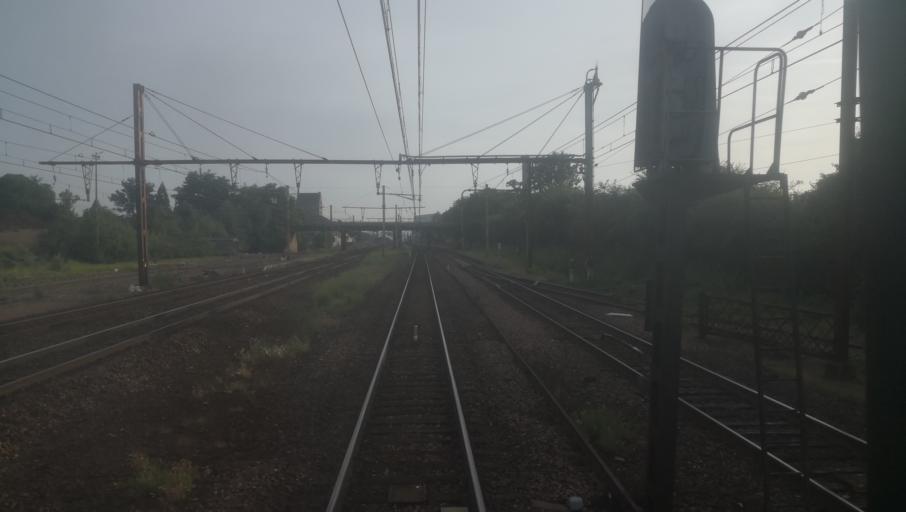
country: FR
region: Centre
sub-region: Departement d'Eure-et-Loir
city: Toury
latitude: 48.1908
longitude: 1.9386
